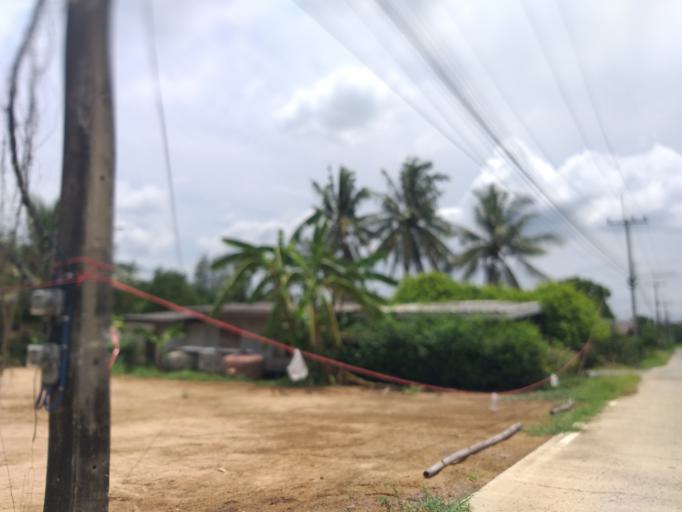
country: TH
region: Pathum Thani
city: Ban Lam Luk Ka
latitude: 13.9872
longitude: 100.8543
